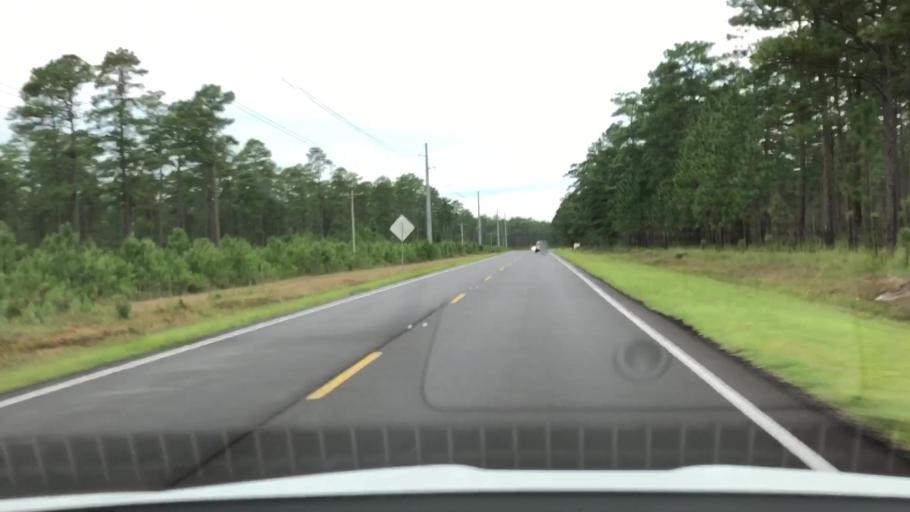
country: US
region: North Carolina
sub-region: Onslow County
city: Swansboro
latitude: 34.8137
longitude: -77.1408
